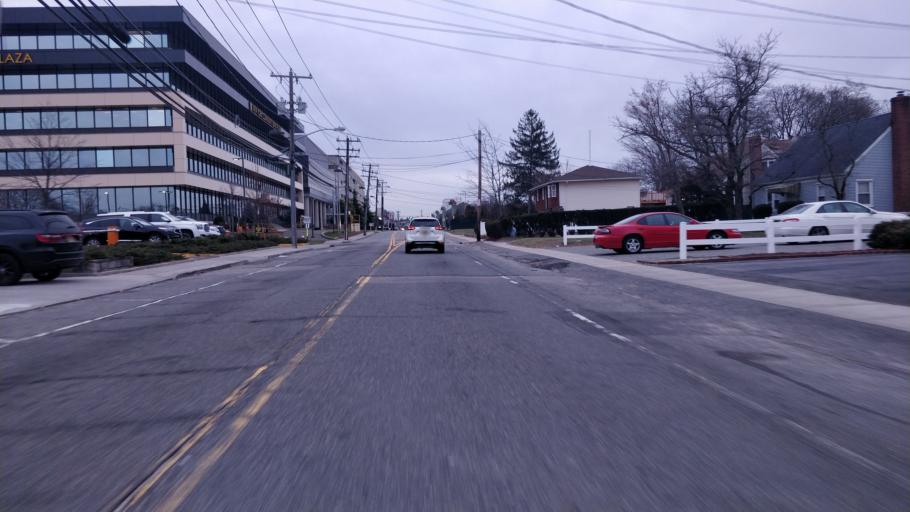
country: US
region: New York
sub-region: Nassau County
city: Hicksville
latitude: 40.7654
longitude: -73.5313
